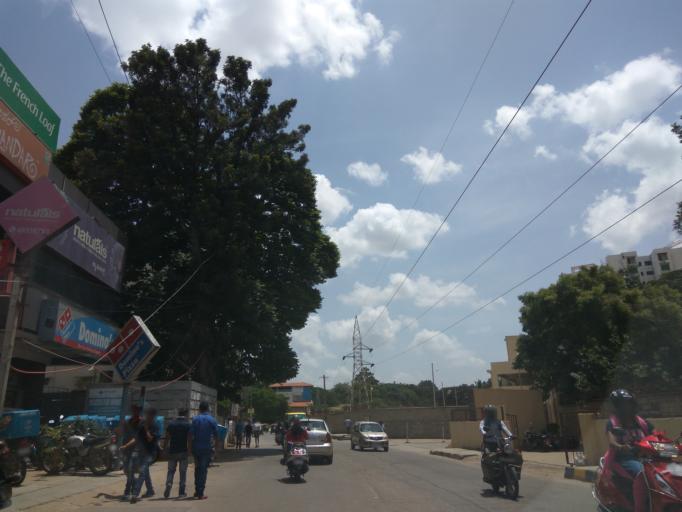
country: IN
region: Karnataka
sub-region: Bangalore Urban
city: Bangalore
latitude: 12.9860
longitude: 77.6689
